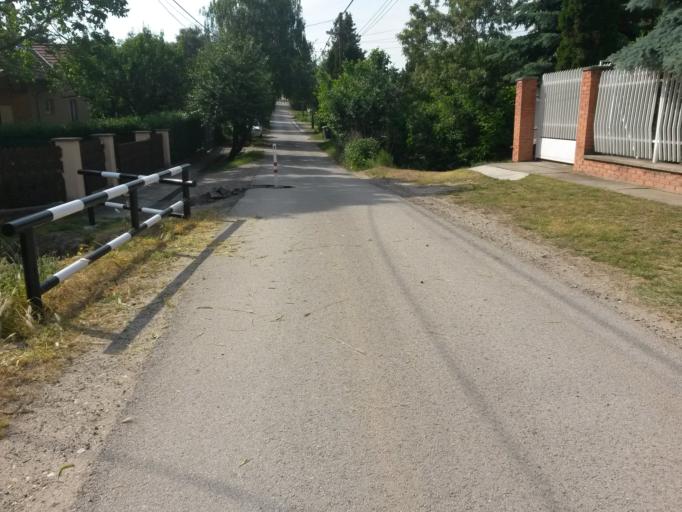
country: HU
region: Pest
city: Kerepes
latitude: 47.5720
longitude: 19.2745
